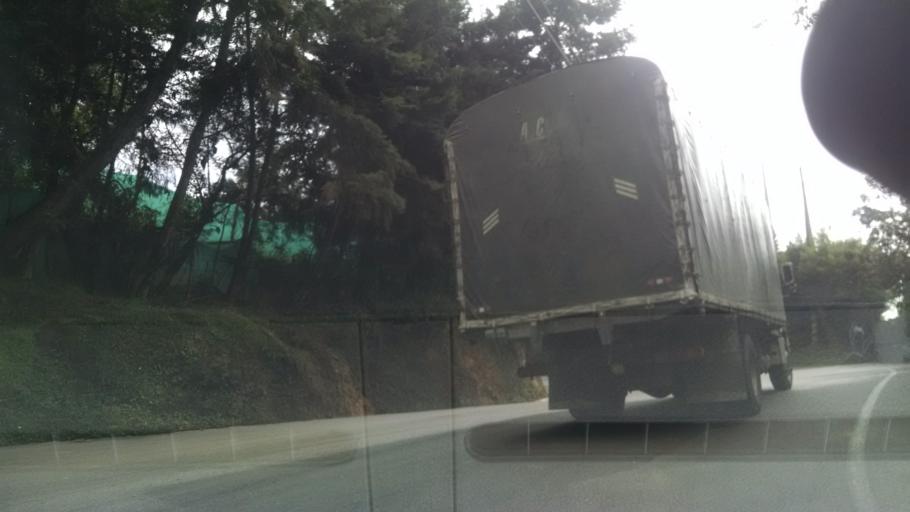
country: CO
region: Antioquia
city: Caldas
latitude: 6.0314
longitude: -75.6233
